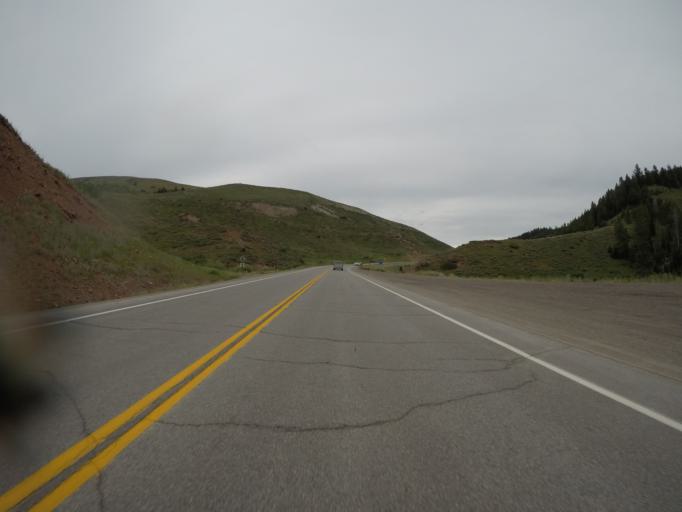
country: US
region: Wyoming
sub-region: Lincoln County
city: Afton
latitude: 42.4880
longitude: -110.9420
